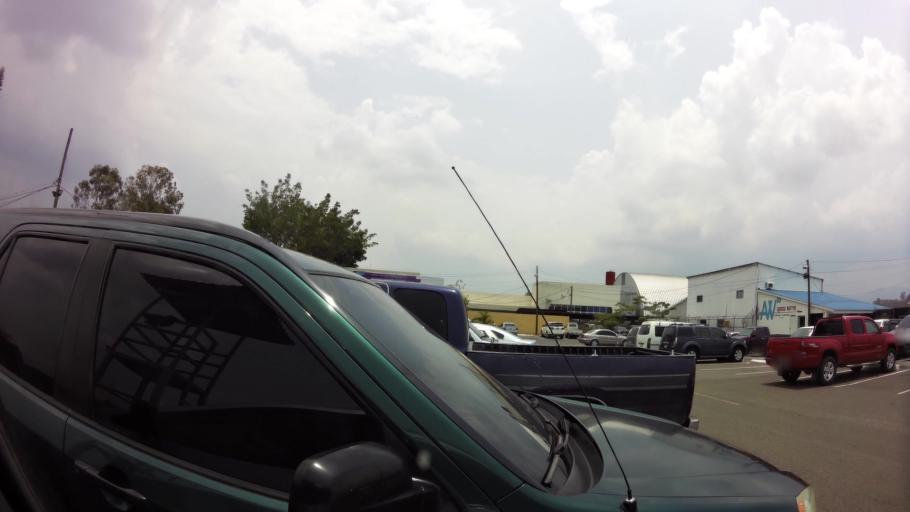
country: HN
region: Francisco Morazan
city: Tegucigalpa
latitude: 14.0620
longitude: -87.2189
